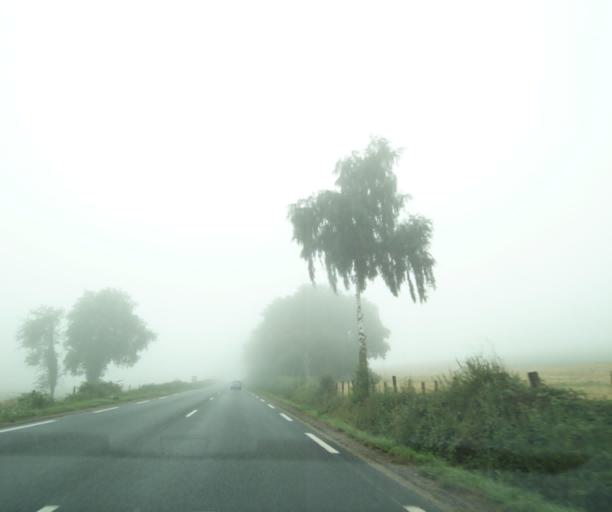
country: FR
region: Midi-Pyrenees
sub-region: Departement de l'Aveyron
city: Baraqueville
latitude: 44.2586
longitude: 2.4162
